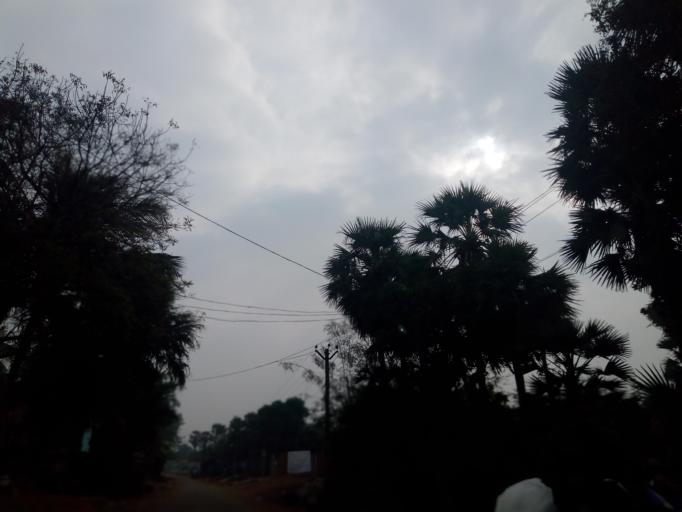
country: IN
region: Andhra Pradesh
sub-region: West Godavari
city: Tadepallegudem
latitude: 16.8635
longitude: 81.3272
